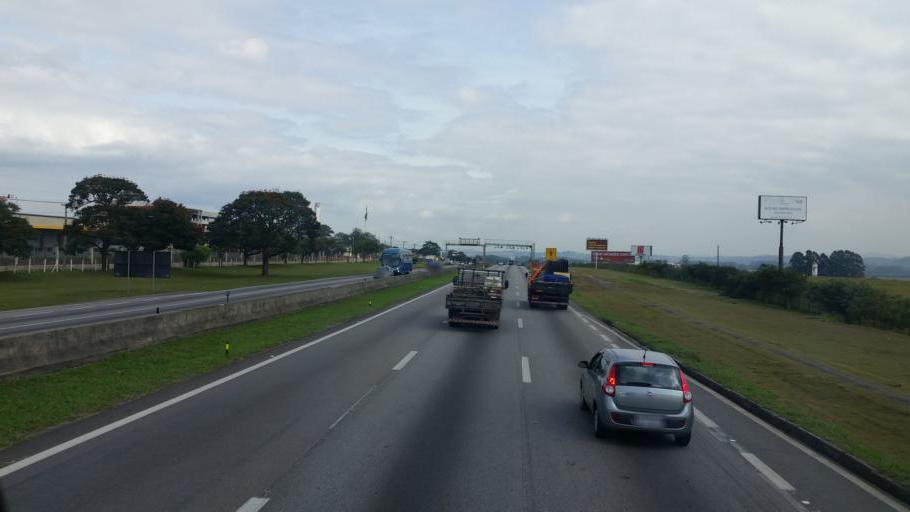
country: BR
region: Sao Paulo
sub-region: Jacarei
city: Jacarei
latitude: -23.2507
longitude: -45.9364
